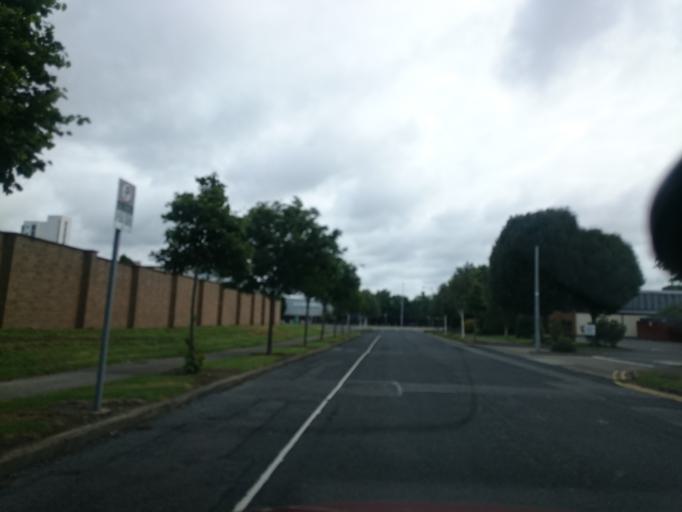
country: IE
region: Leinster
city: Sandyford
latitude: 53.2745
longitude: -6.2153
